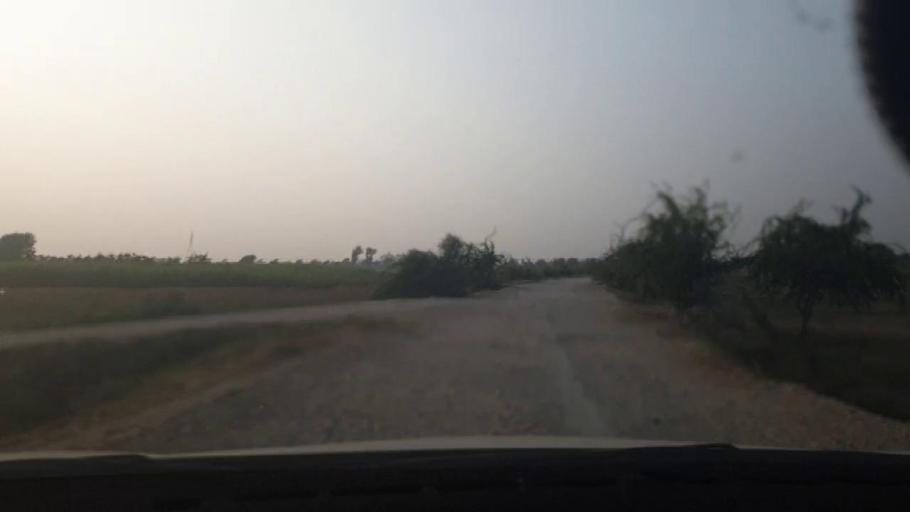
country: PK
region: Sindh
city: Bulri
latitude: 24.8503
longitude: 68.3447
